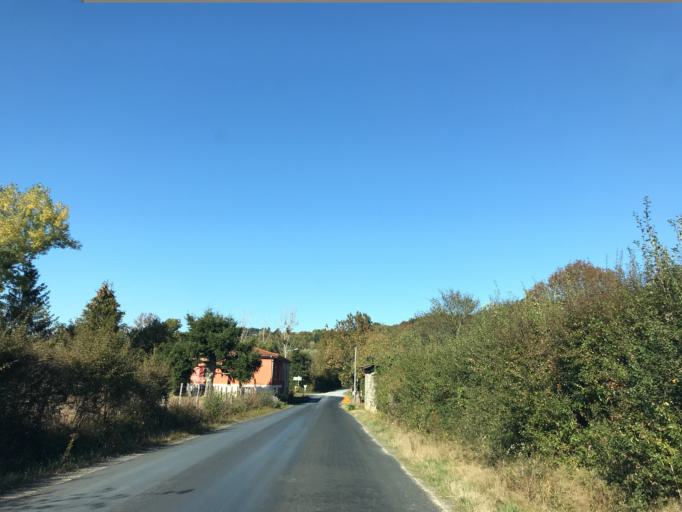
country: FR
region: Auvergne
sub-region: Departement du Puy-de-Dome
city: Courpiere
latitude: 45.7730
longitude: 3.5926
